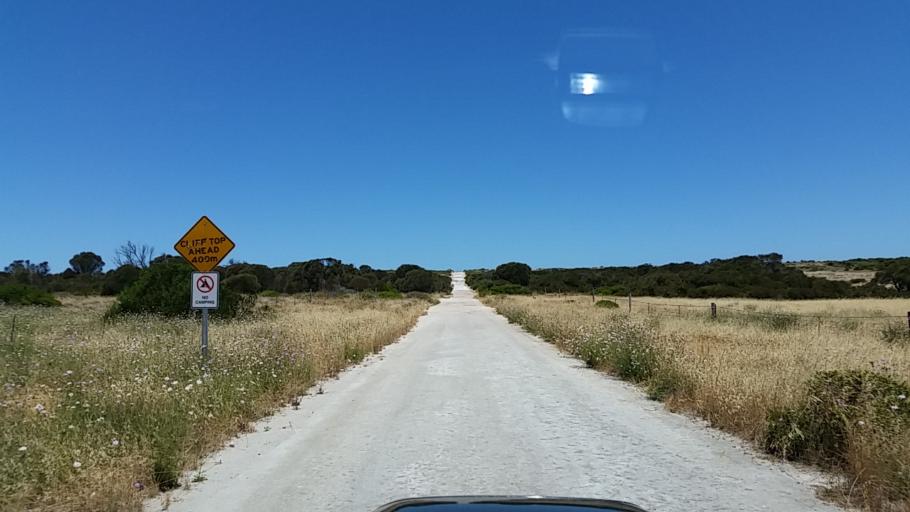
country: AU
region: South Australia
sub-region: Yorke Peninsula
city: Honiton
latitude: -35.2244
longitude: 137.0695
